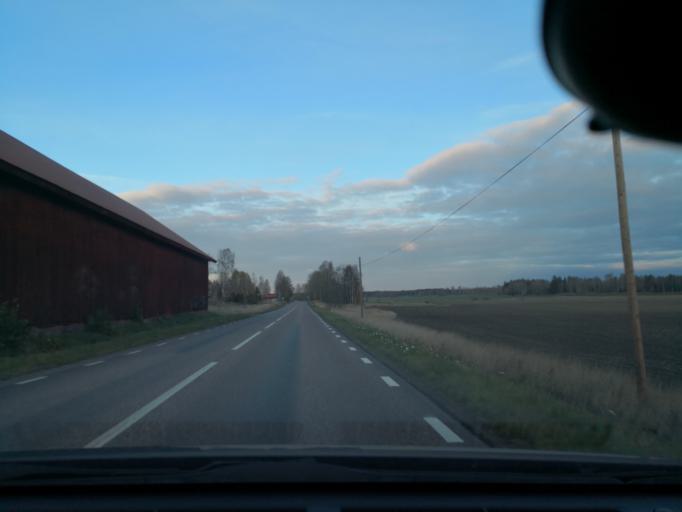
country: SE
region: Vaestmanland
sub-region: Vasteras
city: Tillberga
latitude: 59.6378
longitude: 16.6727
